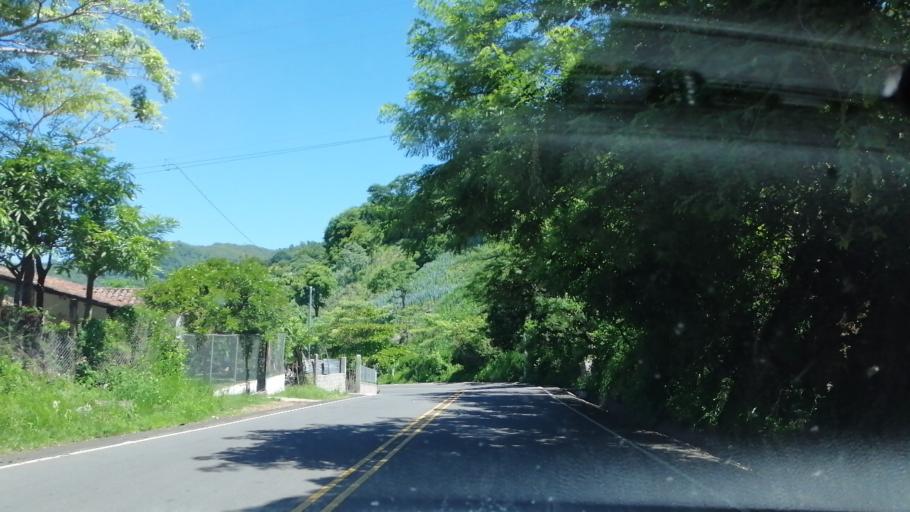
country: SV
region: Morazan
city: Cacaopera
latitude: 13.8130
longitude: -88.1701
